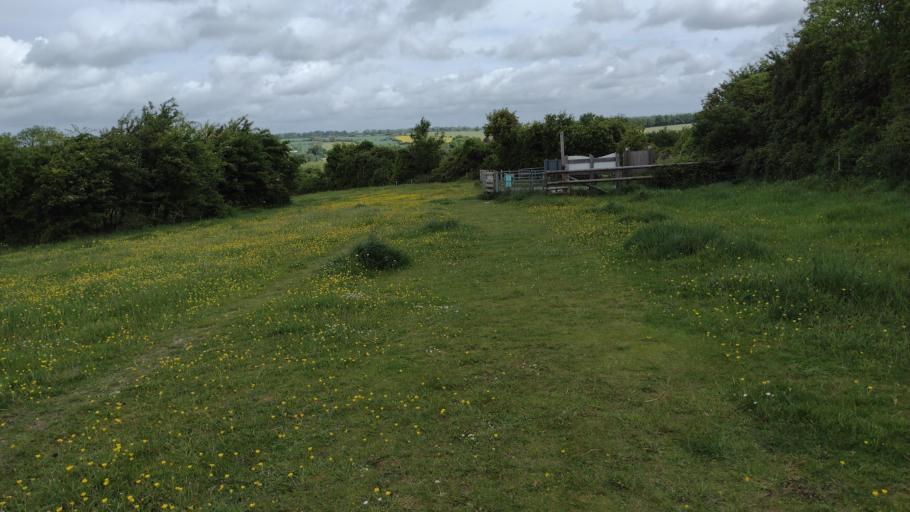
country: GB
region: England
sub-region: Wiltshire
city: Wilton
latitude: 51.0297
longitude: -1.8427
